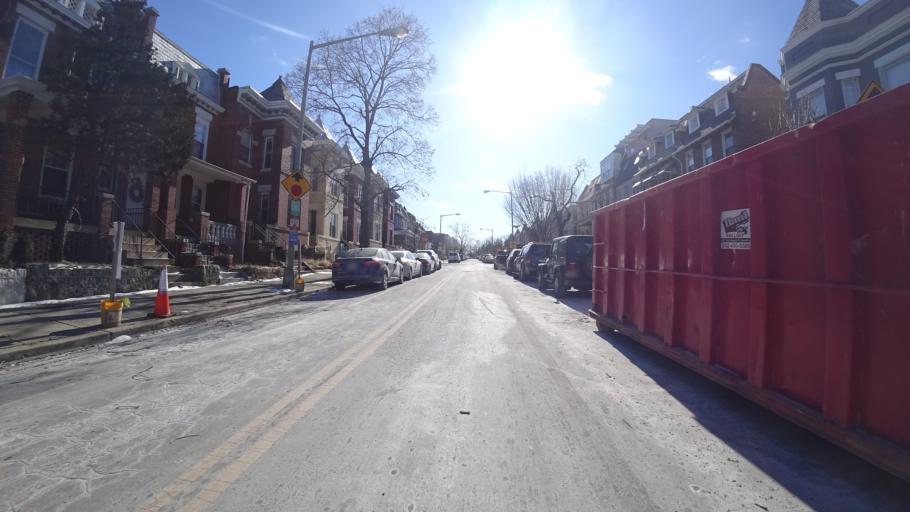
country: US
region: Washington, D.C.
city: Washington, D.C.
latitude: 38.9351
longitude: -77.0285
